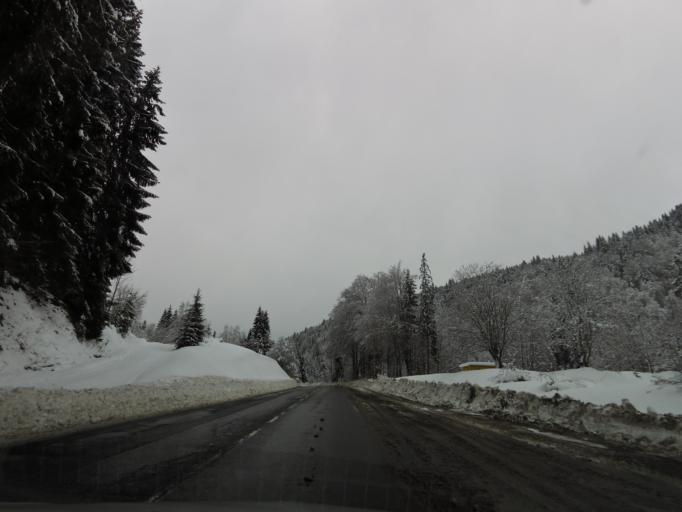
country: FR
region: Rhone-Alpes
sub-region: Departement de la Haute-Savoie
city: Morzine
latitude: 46.1770
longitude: 6.6822
